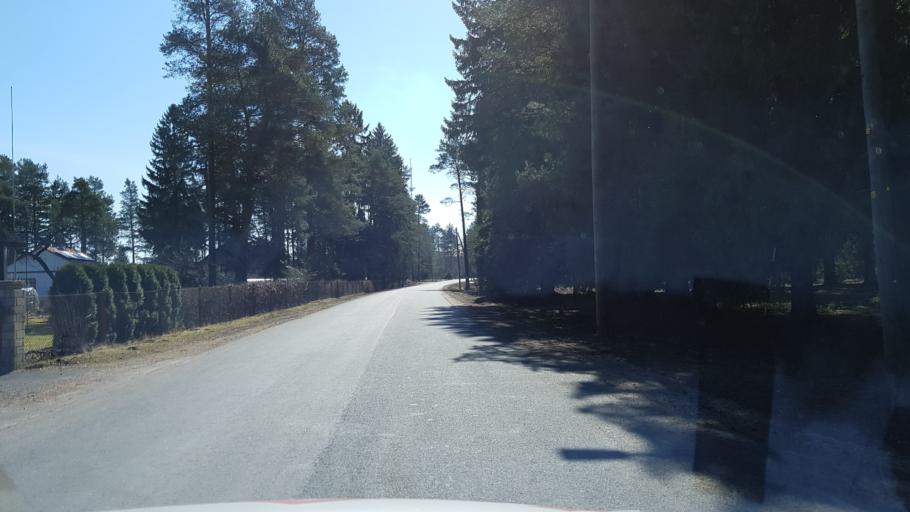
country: EE
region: Ida-Virumaa
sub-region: Kohtla-Nomme vald
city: Kohtla-Nomme
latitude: 59.3608
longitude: 27.1879
